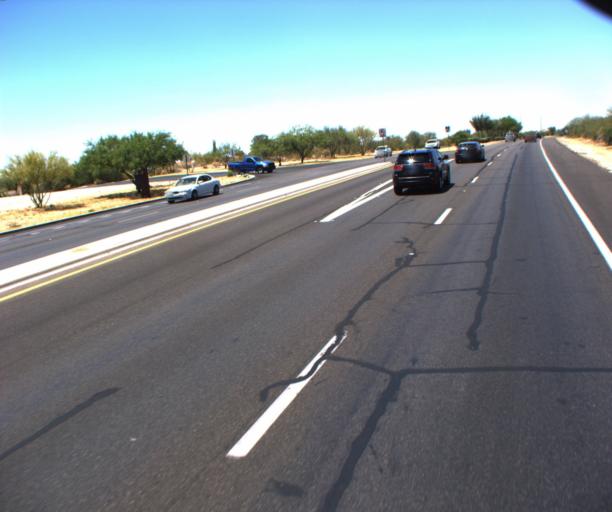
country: US
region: Arizona
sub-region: Pima County
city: Oro Valley
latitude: 32.4243
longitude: -110.9628
